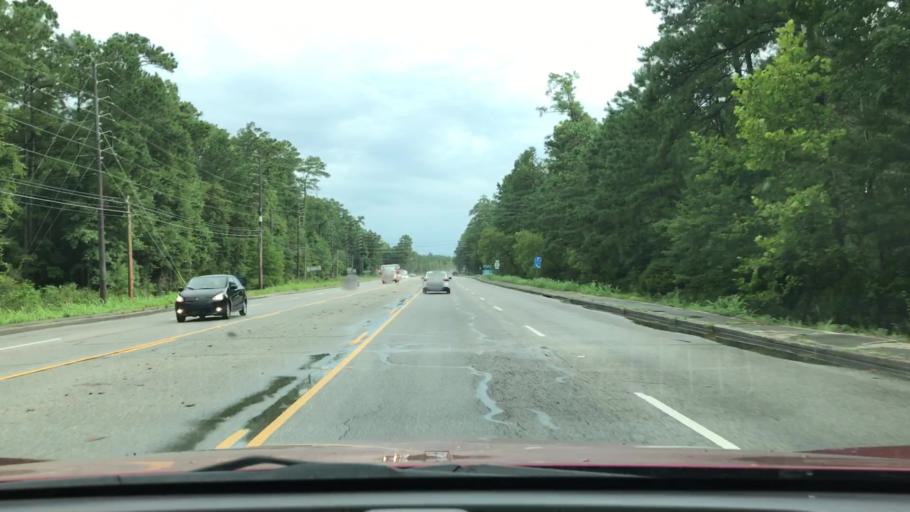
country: US
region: South Carolina
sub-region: Georgetown County
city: Georgetown
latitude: 33.4135
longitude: -79.2851
